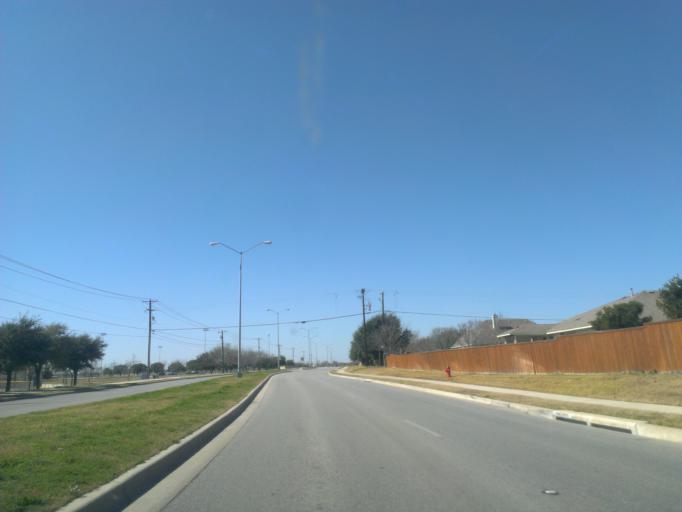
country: US
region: Texas
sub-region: Williamson County
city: Round Rock
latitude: 30.5466
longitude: -97.6209
